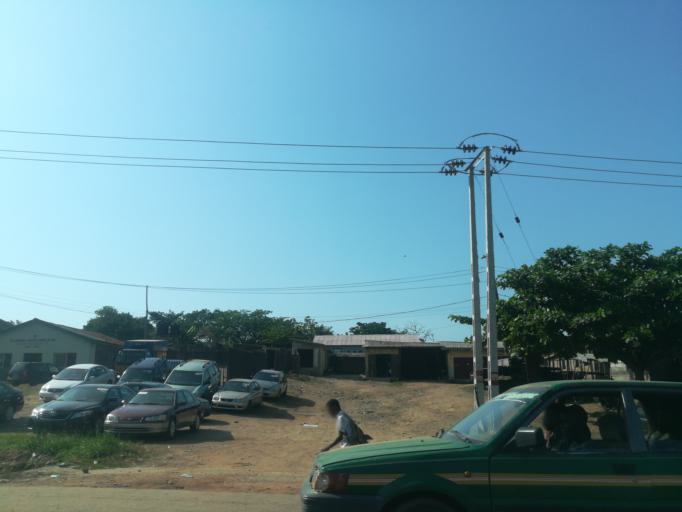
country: NG
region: Ogun
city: Abeokuta
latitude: 7.1391
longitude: 3.3119
